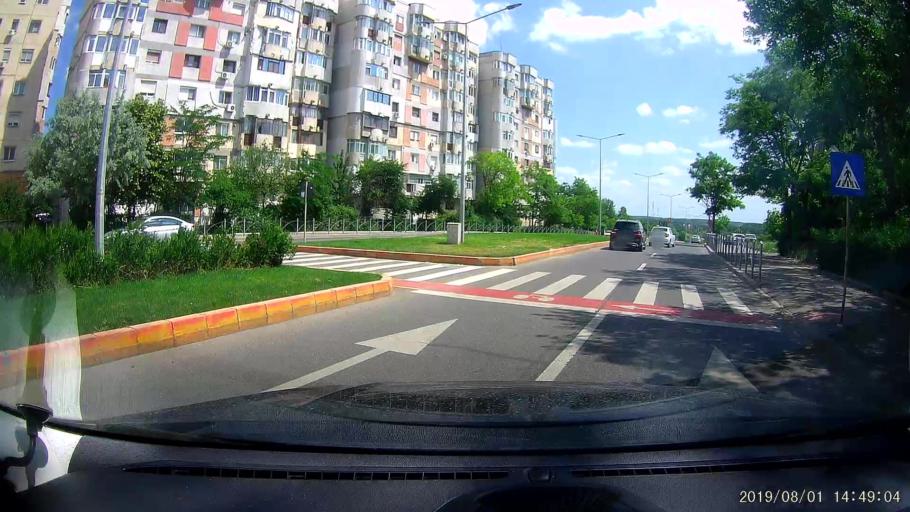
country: RO
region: Galati
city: Galati
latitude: 45.4090
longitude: 28.0151
